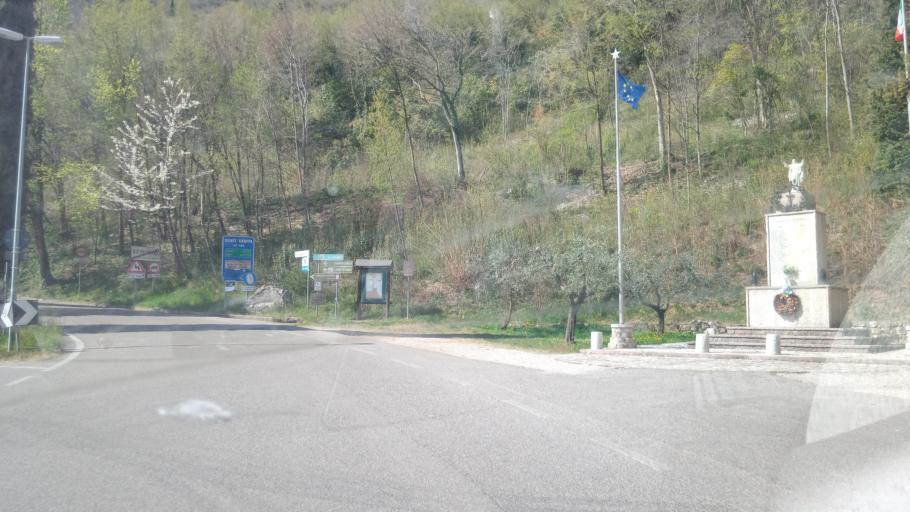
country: IT
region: Veneto
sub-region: Provincia di Treviso
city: Borso del Grappa
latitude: 45.8132
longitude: 11.7707
